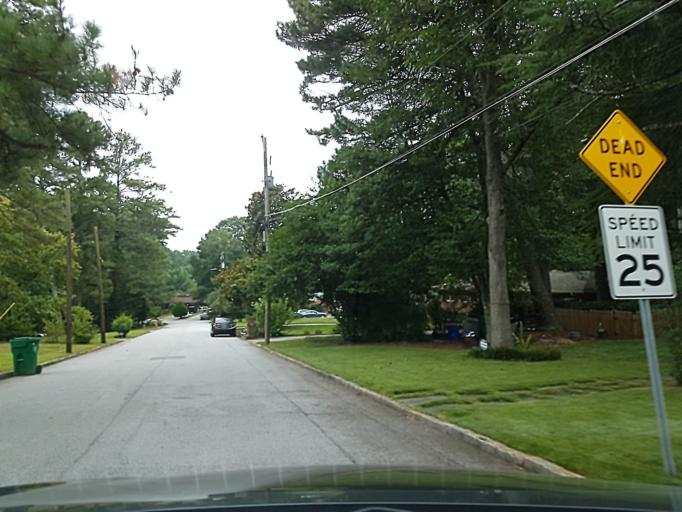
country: US
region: Georgia
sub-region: DeKalb County
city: North Druid Hills
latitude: 33.8299
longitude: -84.3127
